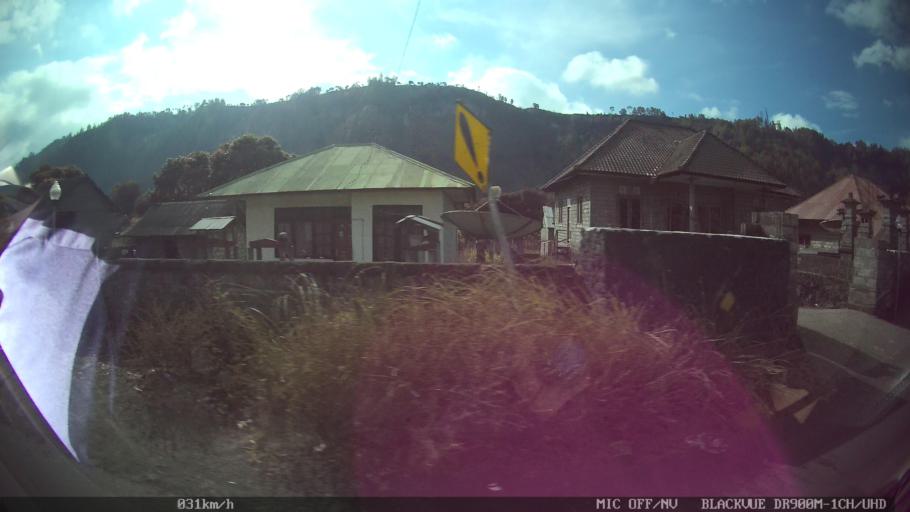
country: ID
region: Bali
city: Banjar Kedisan
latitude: -8.2163
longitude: 115.3686
